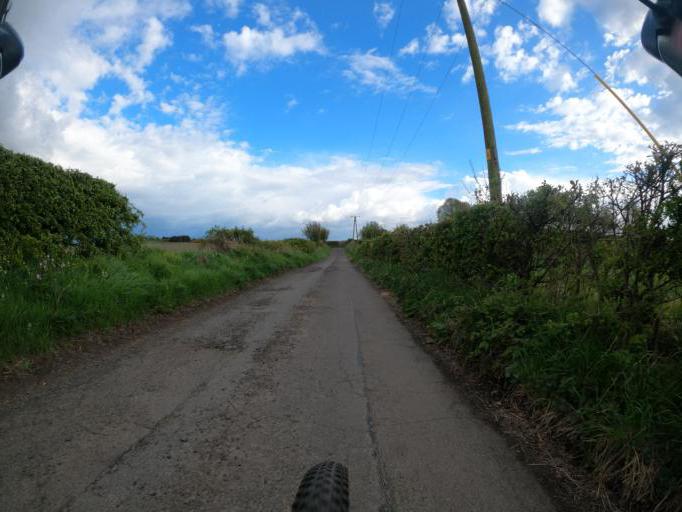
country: GB
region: Scotland
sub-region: Edinburgh
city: Ratho
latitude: 55.9574
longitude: -3.3379
